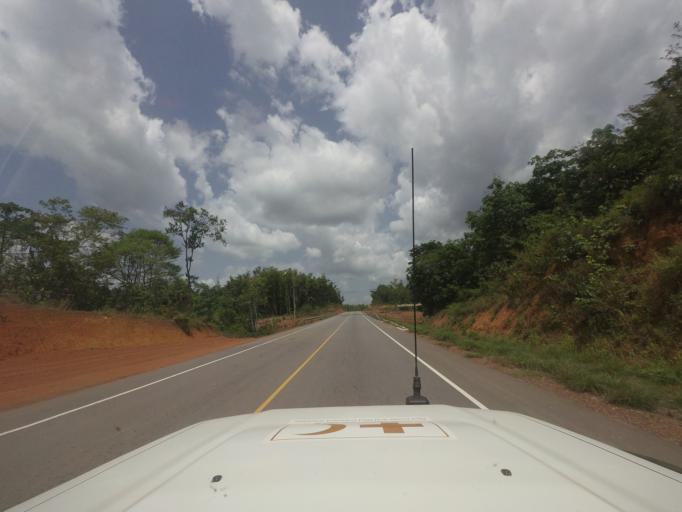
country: LR
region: Bong
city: Gbarnga
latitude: 7.0529
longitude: -9.2312
